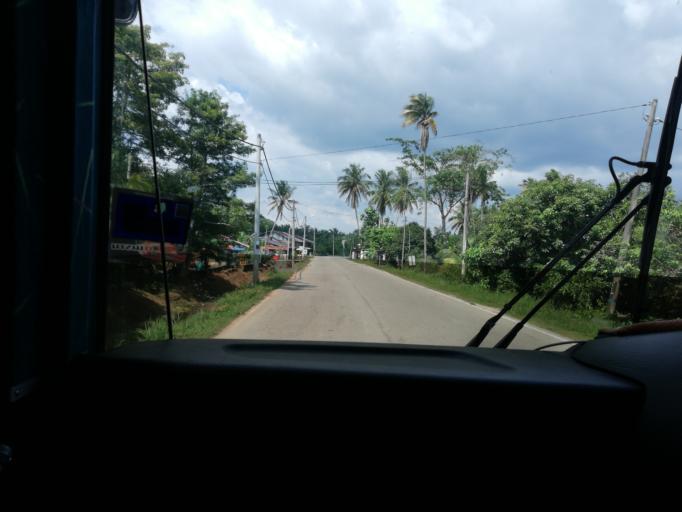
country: MY
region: Perak
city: Parit Buntar
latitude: 5.1176
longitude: 100.5611
